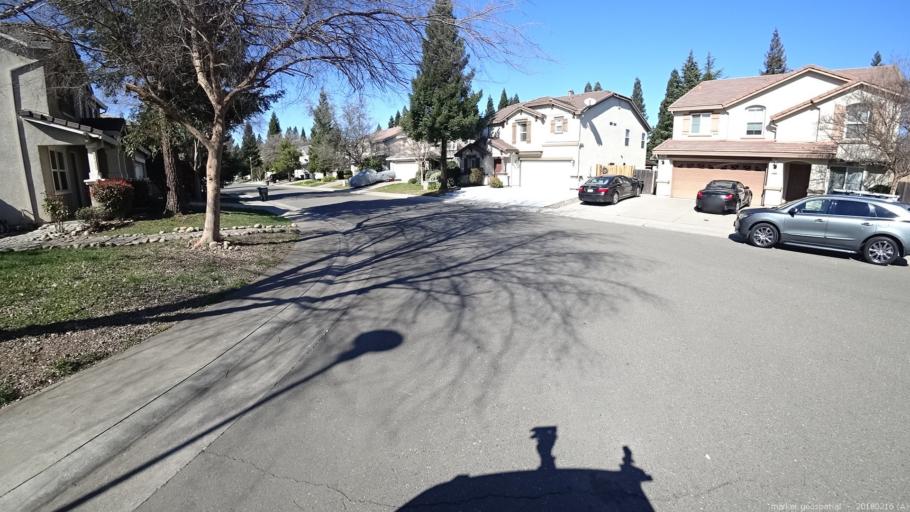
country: US
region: California
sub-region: Sacramento County
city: Gold River
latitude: 38.6181
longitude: -121.2476
